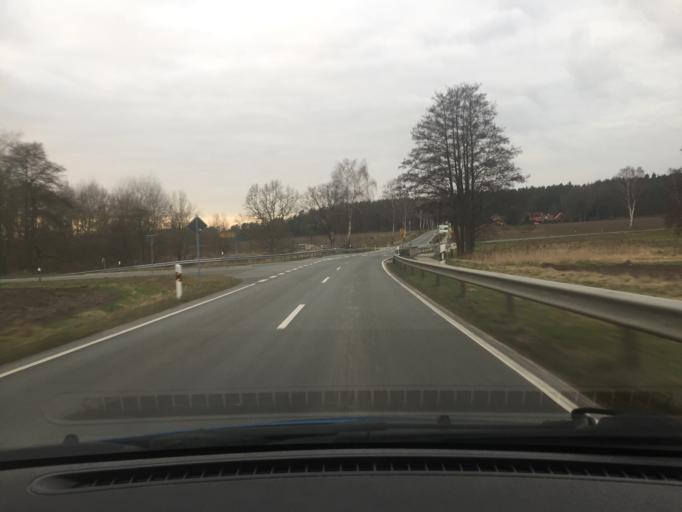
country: DE
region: Lower Saxony
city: Bad Bevensen
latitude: 53.0577
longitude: 10.6114
